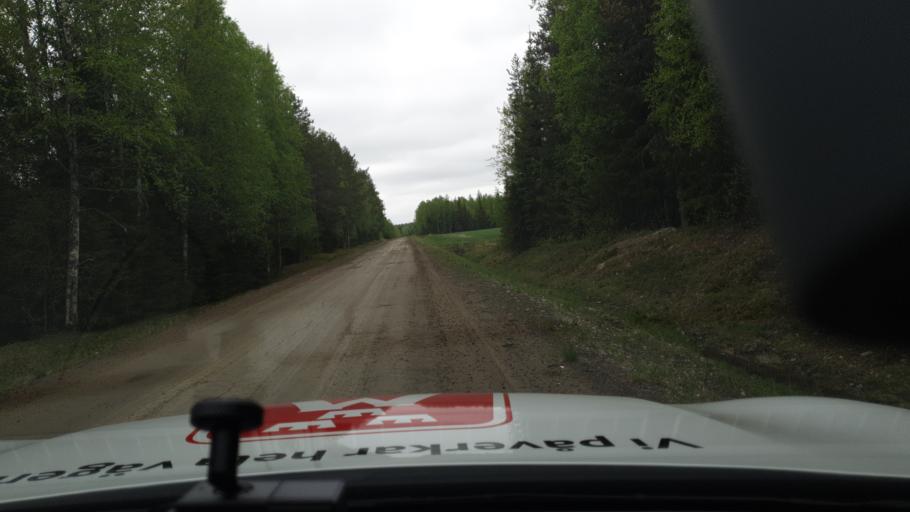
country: SE
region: Vaesterbotten
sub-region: Vannas Kommun
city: Vannasby
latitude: 64.0380
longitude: 19.8992
